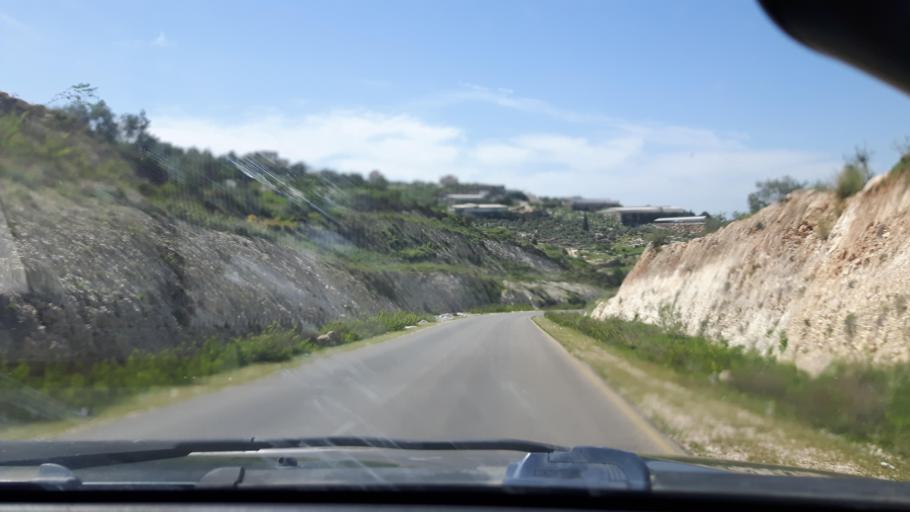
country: PS
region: West Bank
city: Kharbatha al Misbah
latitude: 31.8776
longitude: 35.0759
